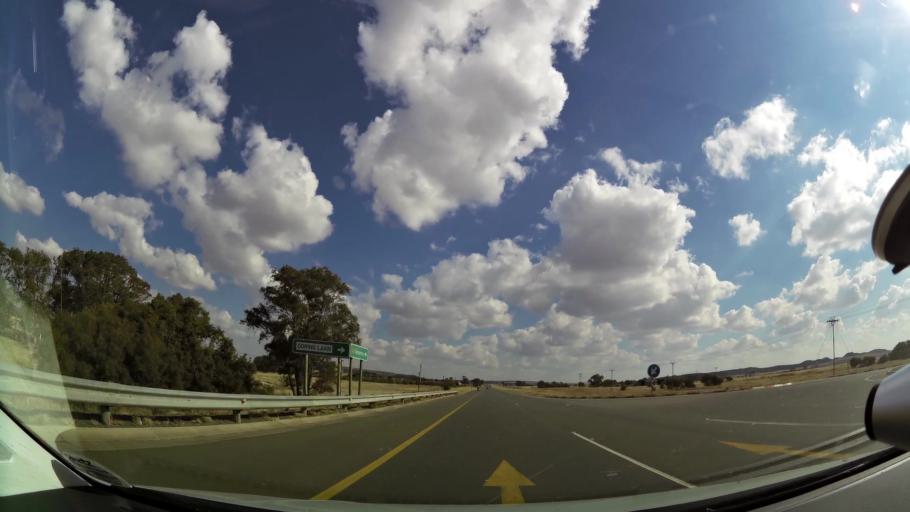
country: ZA
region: Orange Free State
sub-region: Mangaung Metropolitan Municipality
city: Bloemfontein
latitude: -29.1407
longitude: 26.1058
